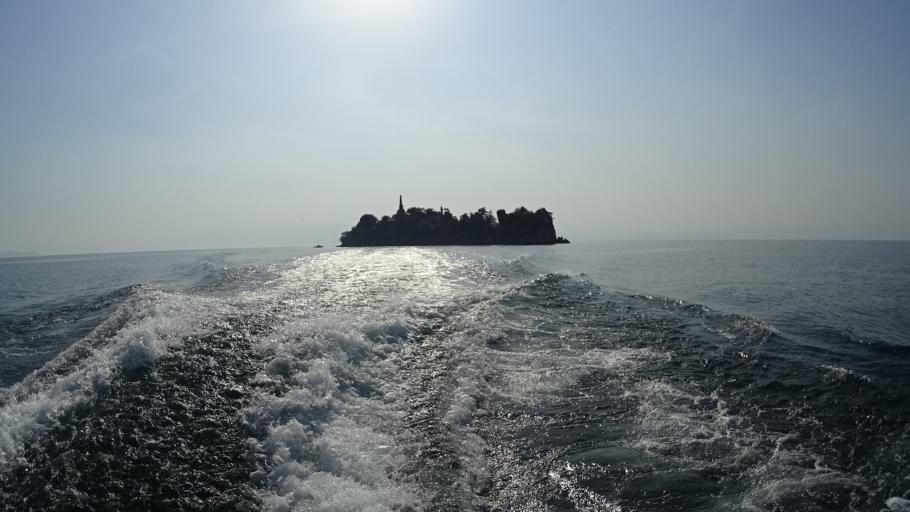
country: JP
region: Shiga Prefecture
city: Hikone
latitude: 35.2964
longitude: 136.1821
